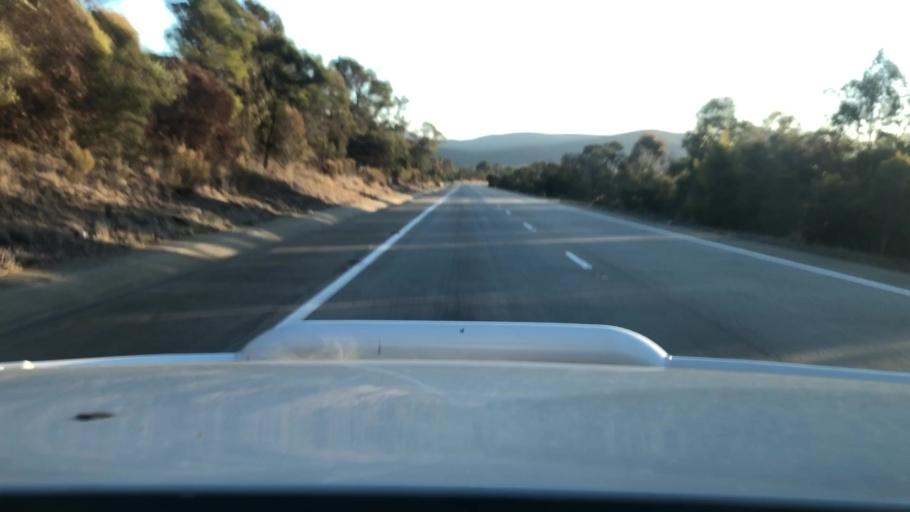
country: AU
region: New South Wales
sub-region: Goulburn Mulwaree
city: Goulburn
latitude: -34.7500
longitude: 149.7688
